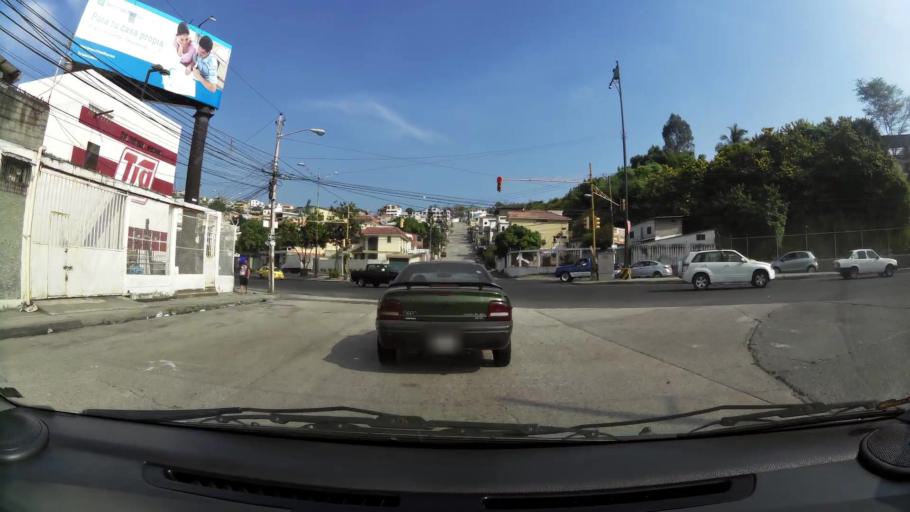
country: EC
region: Guayas
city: Guayaquil
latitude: -2.1801
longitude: -79.9104
